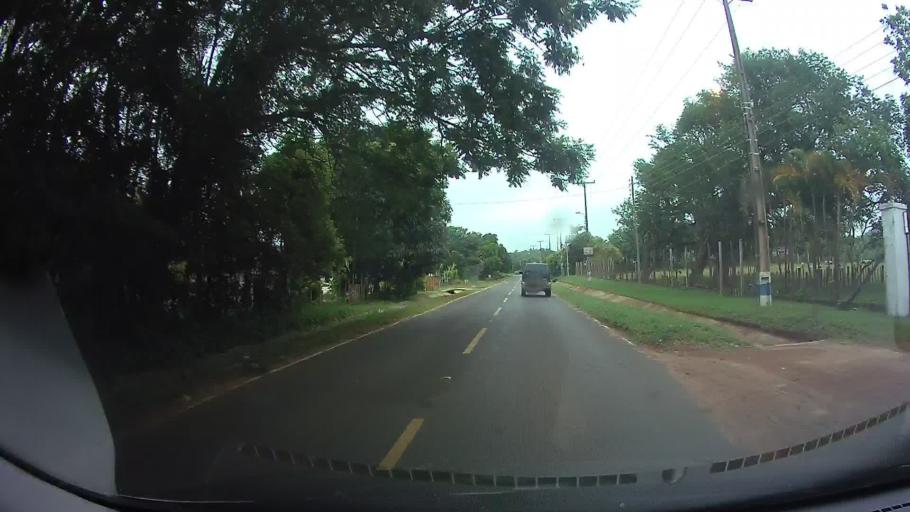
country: PY
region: Central
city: Itaugua
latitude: -25.3530
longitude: -57.3403
